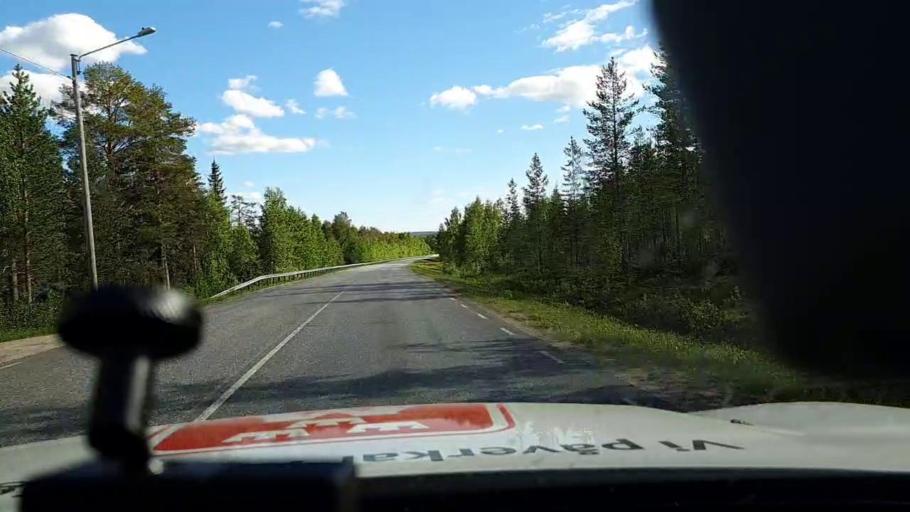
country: SE
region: Norrbotten
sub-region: Overtornea Kommun
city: OEvertornea
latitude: 66.3472
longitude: 23.6483
